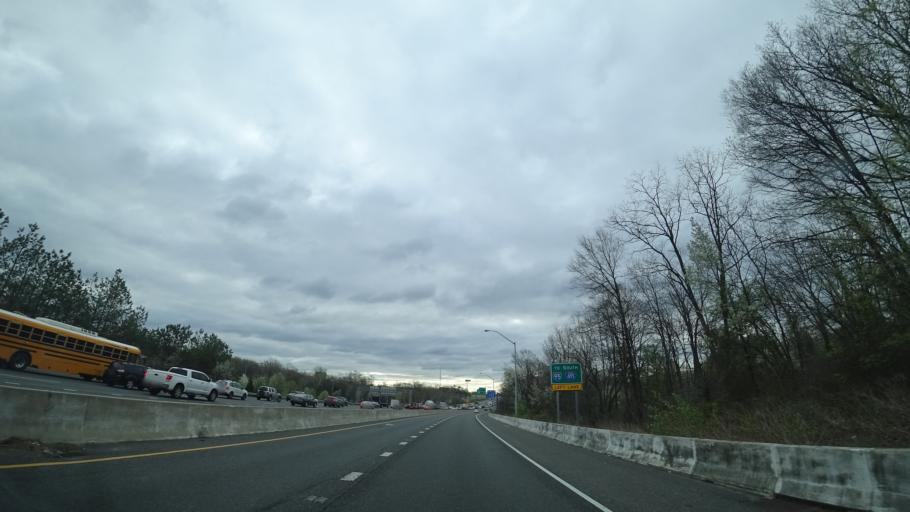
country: US
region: Maryland
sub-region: Prince George's County
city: Beltsville
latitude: 39.0212
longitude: -76.9381
